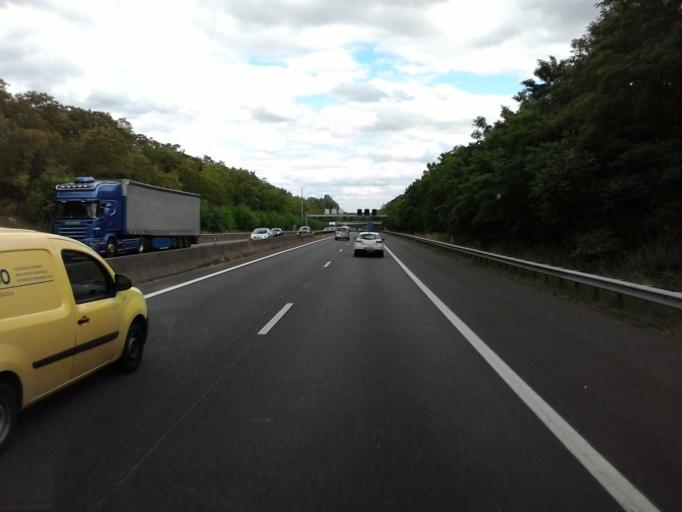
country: LU
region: Luxembourg
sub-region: Canton de Capellen
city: Mamer
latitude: 49.6360
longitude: 6.0268
